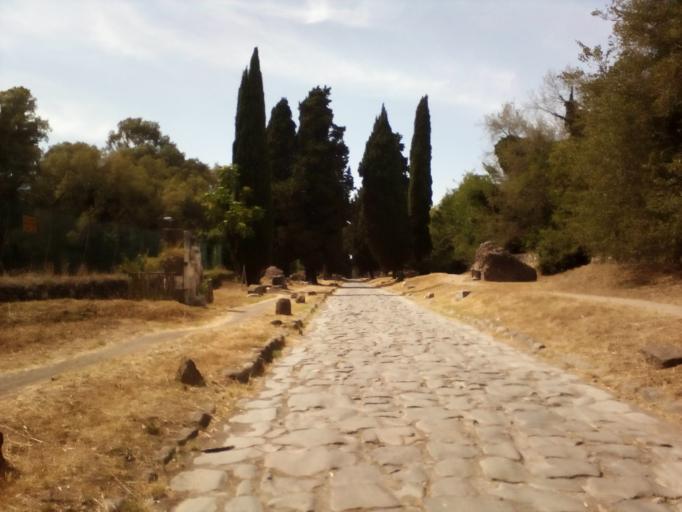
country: IT
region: Latium
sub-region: Citta metropolitana di Roma Capitale
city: Rome
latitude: 41.8421
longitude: 12.5319
